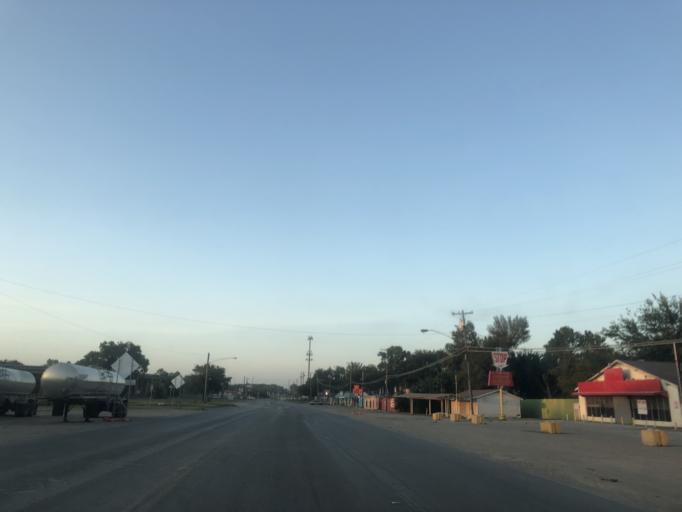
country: US
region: Texas
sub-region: Dallas County
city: Dallas
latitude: 32.7410
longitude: -96.7585
